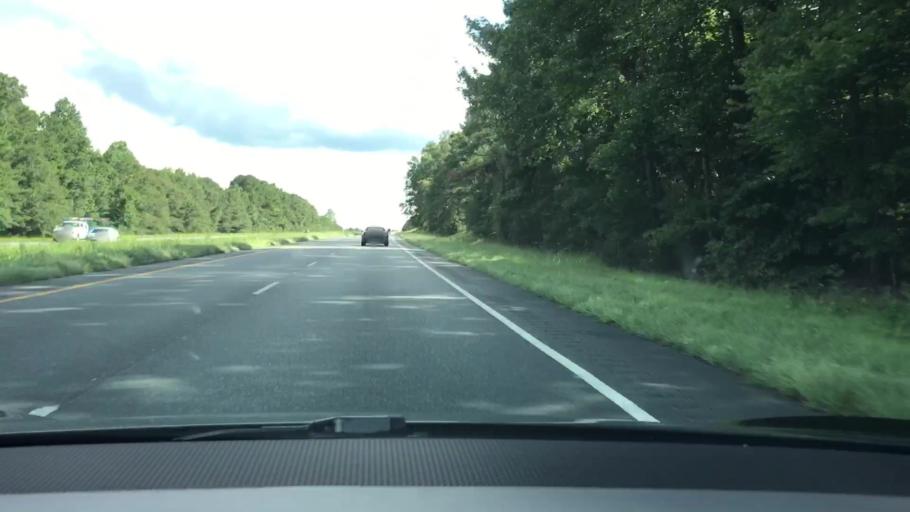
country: US
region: Alabama
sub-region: Pike County
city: Troy
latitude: 31.9074
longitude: -86.0120
